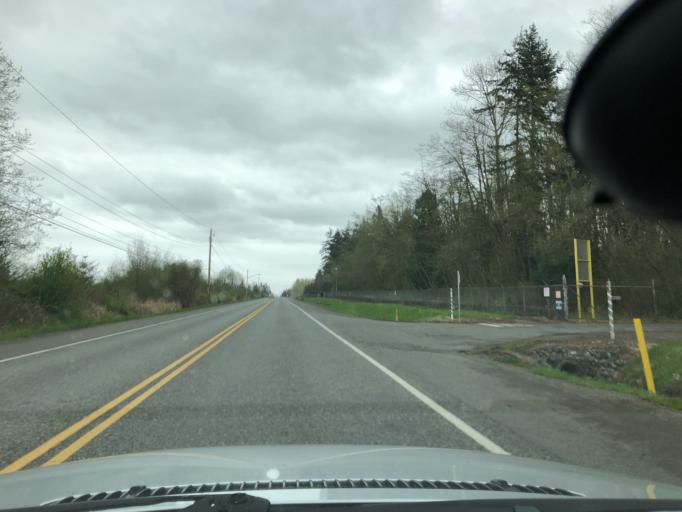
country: US
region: Washington
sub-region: Whatcom County
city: Birch Bay
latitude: 48.8922
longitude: -122.7368
